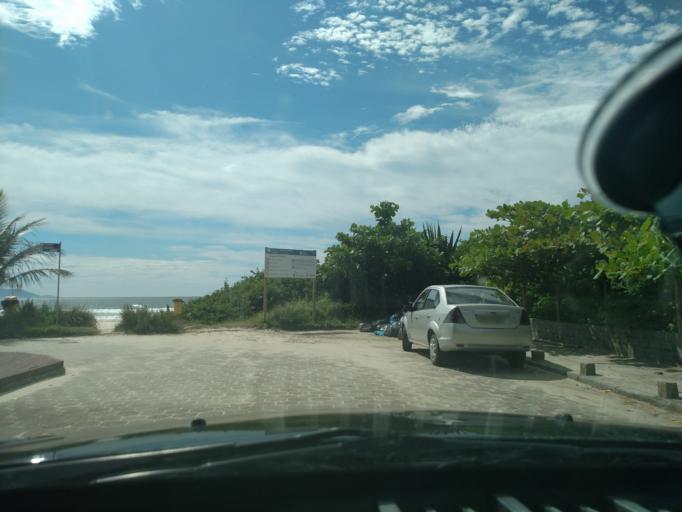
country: BR
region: Santa Catarina
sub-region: Tijucas
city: Tijucas
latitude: -27.3224
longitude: -48.5397
